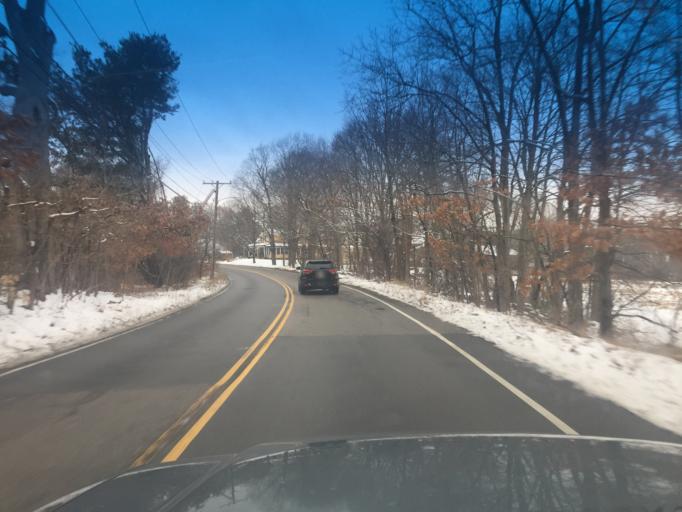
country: US
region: Massachusetts
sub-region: Norfolk County
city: Millis
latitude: 42.1827
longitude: -71.3631
